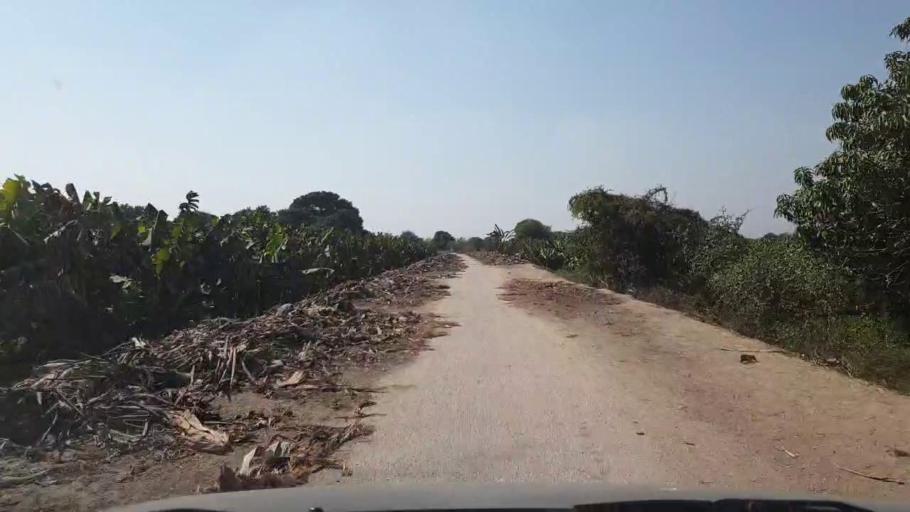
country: PK
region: Sindh
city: Tando Allahyar
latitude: 25.4289
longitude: 68.6444
